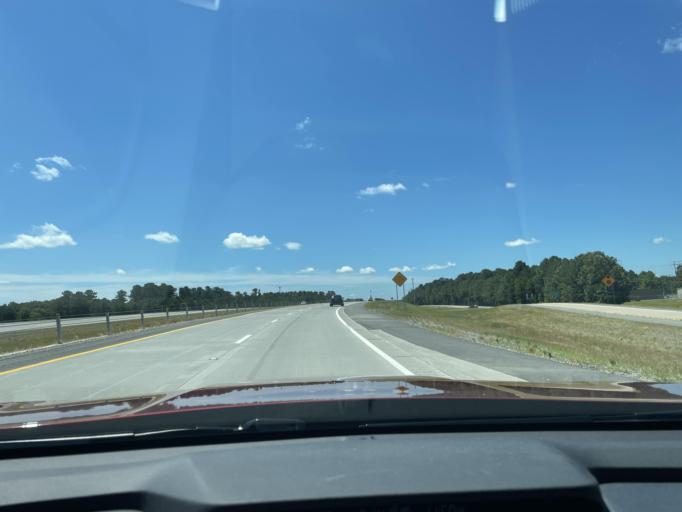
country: US
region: Arkansas
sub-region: Jefferson County
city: White Hall
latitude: 34.2182
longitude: -92.0715
